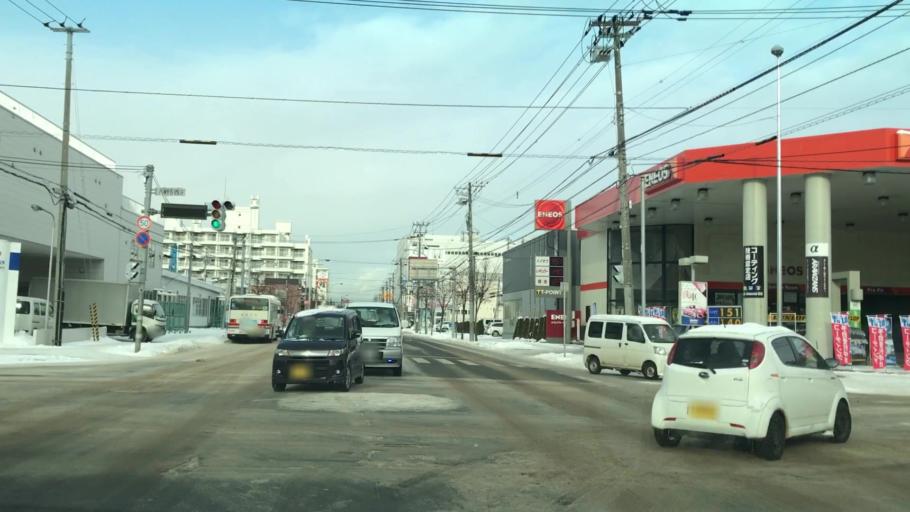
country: JP
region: Hokkaido
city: Sapporo
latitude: 43.0938
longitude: 141.3036
